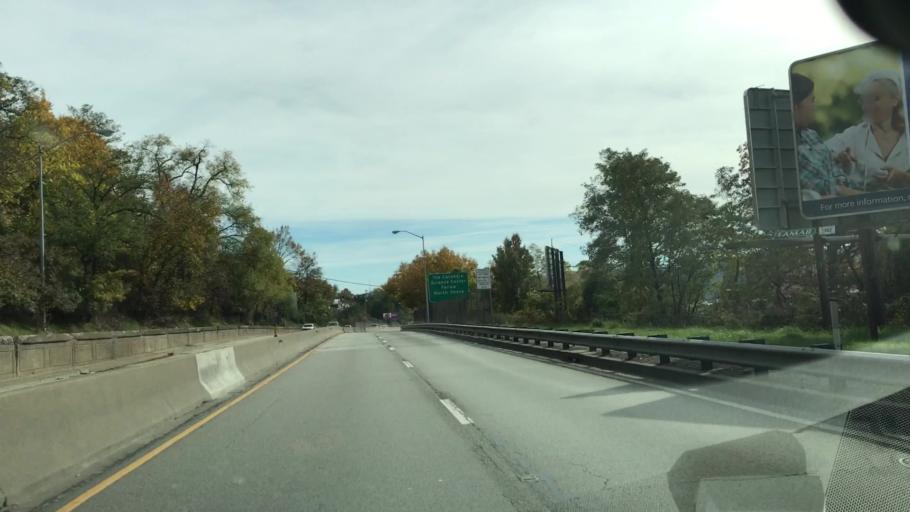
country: US
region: Pennsylvania
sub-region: Allegheny County
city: Bellevue
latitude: 40.4738
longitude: -80.0391
